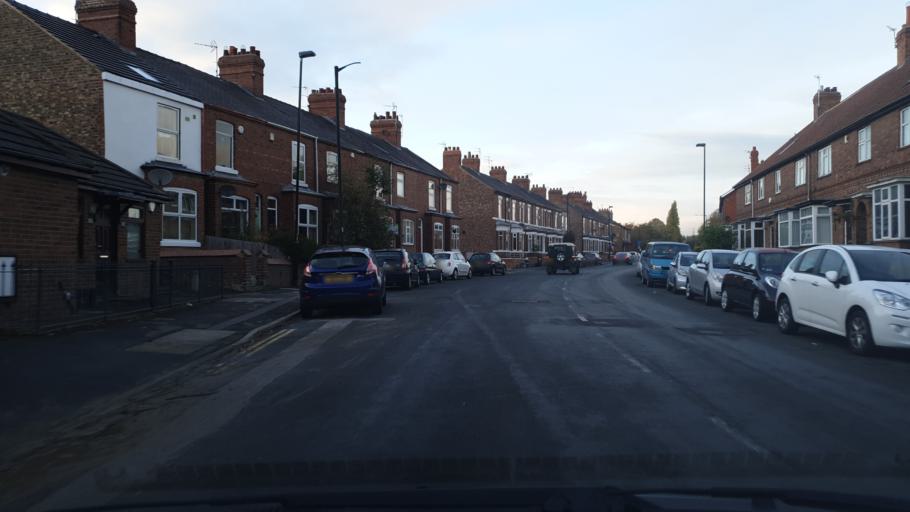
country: GB
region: England
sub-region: City of York
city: York
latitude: 53.9719
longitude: -1.0738
